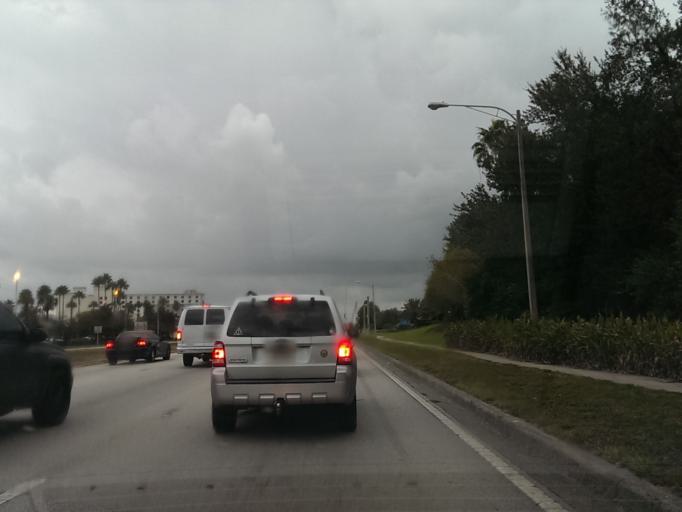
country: US
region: Florida
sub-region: Orange County
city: Tangelo Park
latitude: 28.4801
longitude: -81.4589
